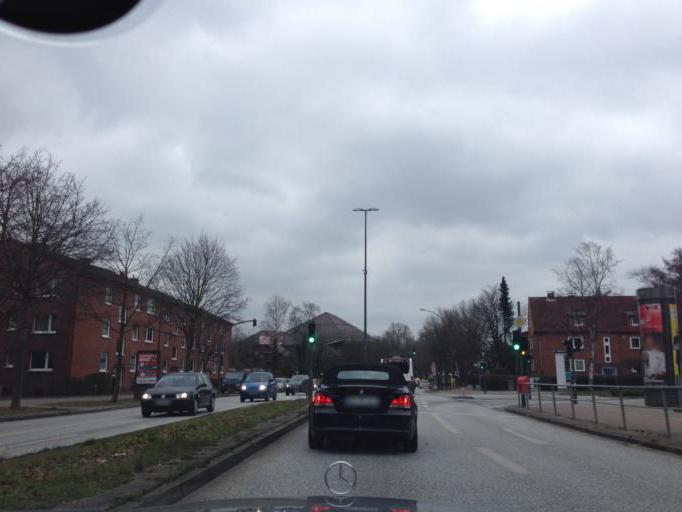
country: DE
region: Hamburg
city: Farmsen-Berne
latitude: 53.6013
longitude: 10.1285
